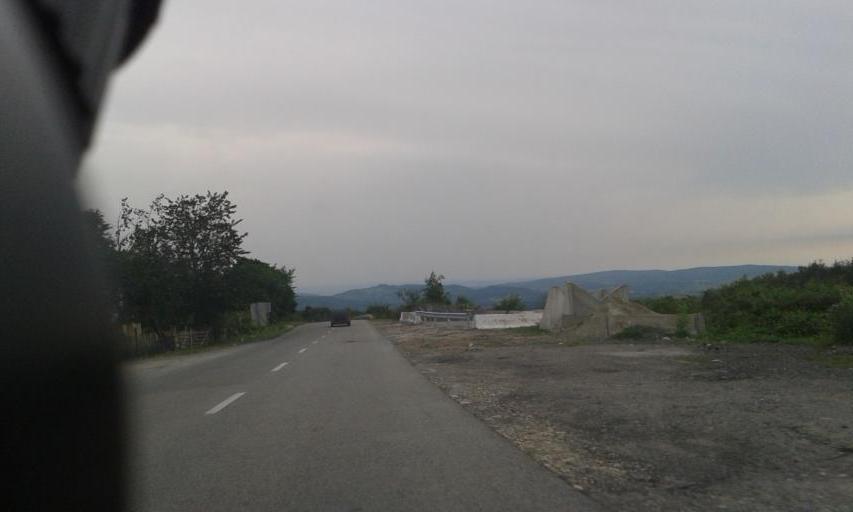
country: RO
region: Gorj
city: Novaci-Straini
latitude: 45.1937
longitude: 23.6860
